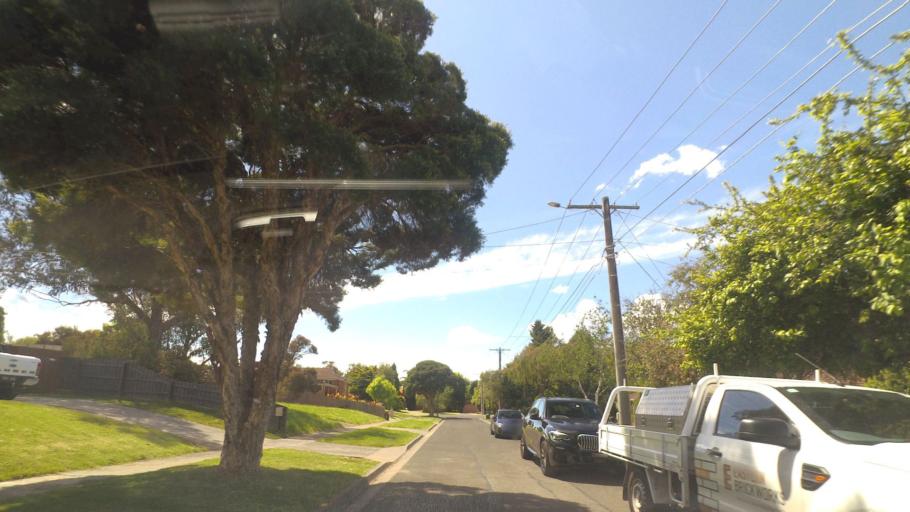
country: AU
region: Victoria
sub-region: Maroondah
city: Croydon South
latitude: -37.8218
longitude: 145.2758
